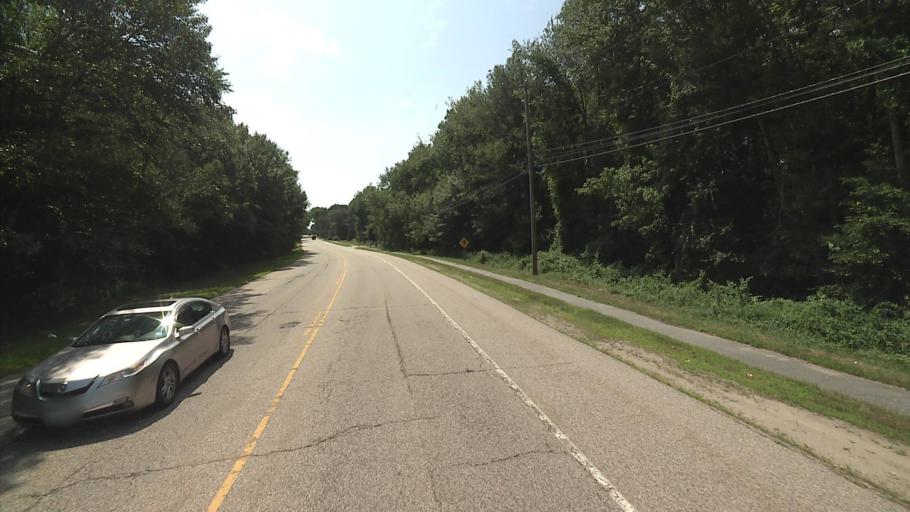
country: US
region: Connecticut
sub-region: New London County
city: Central Waterford
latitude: 41.3315
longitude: -72.1357
